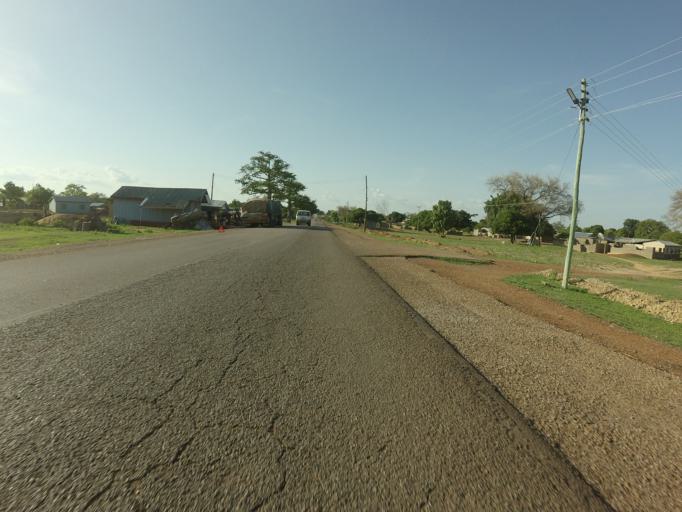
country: GH
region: Upper East
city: Navrongo
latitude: 10.9127
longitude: -1.0900
